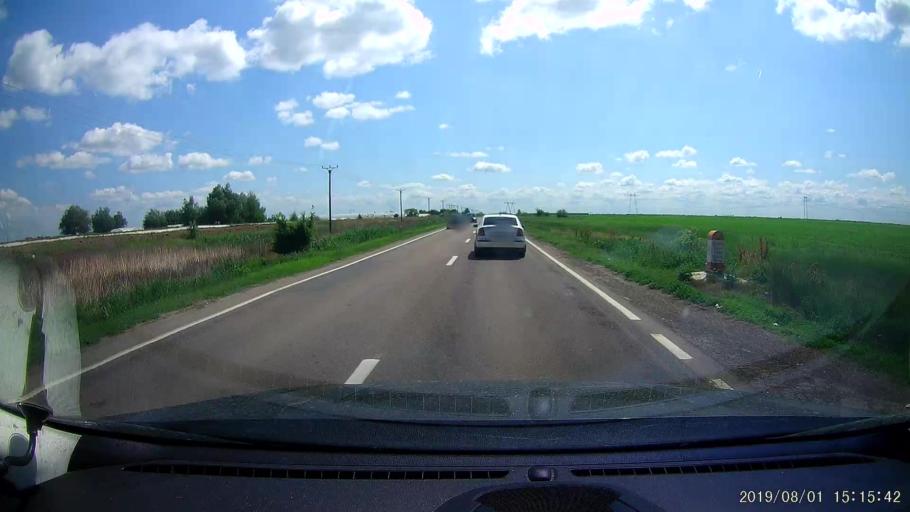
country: RO
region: Braila
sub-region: Comuna Tichilesti
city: Tichilesti
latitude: 45.1601
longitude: 27.8645
